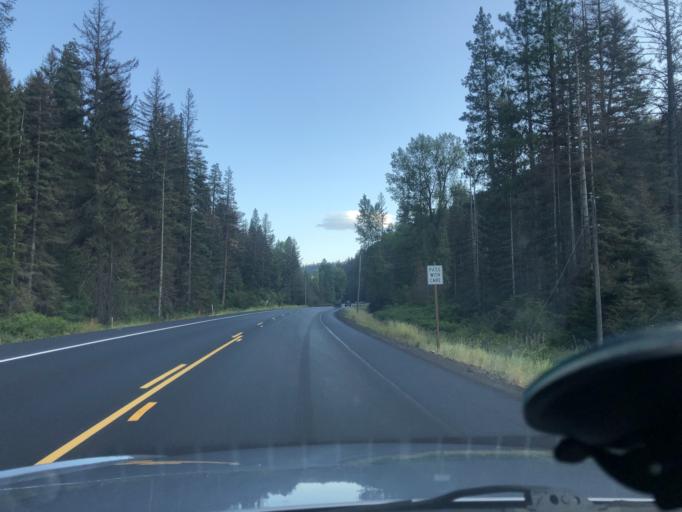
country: US
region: Washington
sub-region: Kittitas County
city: Cle Elum
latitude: 47.2797
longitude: -120.6977
